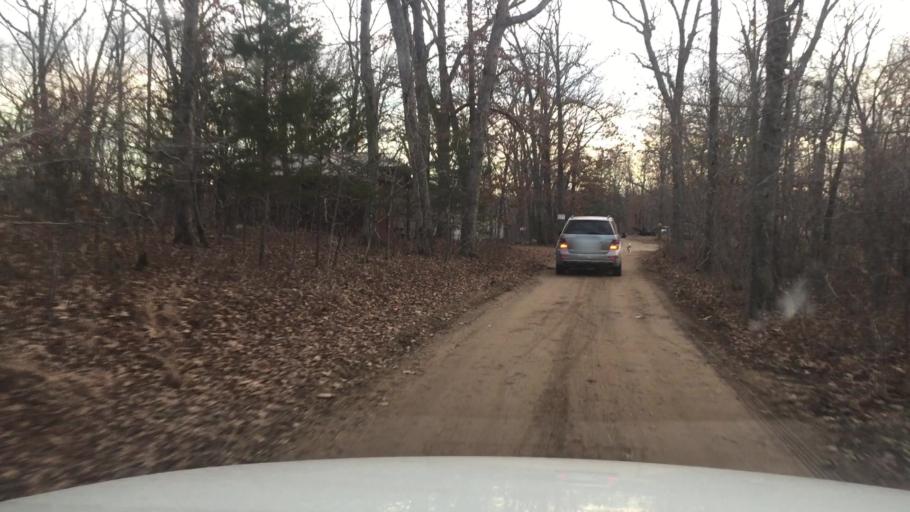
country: US
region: Missouri
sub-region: Camden County
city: Four Seasons
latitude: 38.3092
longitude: -92.7504
